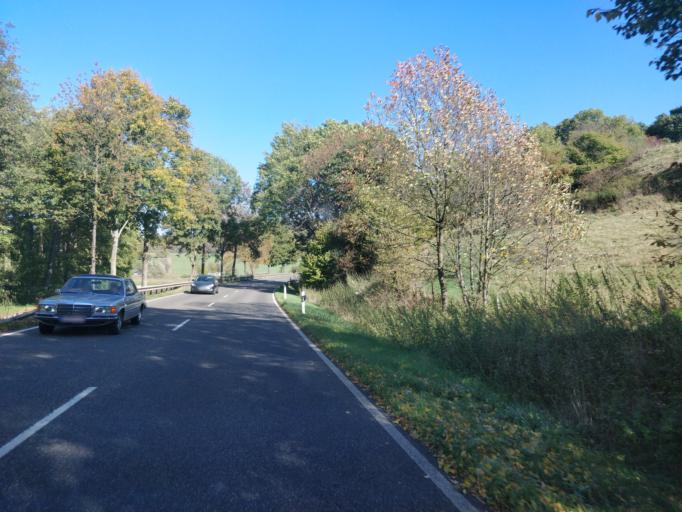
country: DE
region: North Rhine-Westphalia
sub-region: Regierungsbezirk Koln
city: Bad Munstereifel
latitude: 50.5498
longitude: 6.7169
